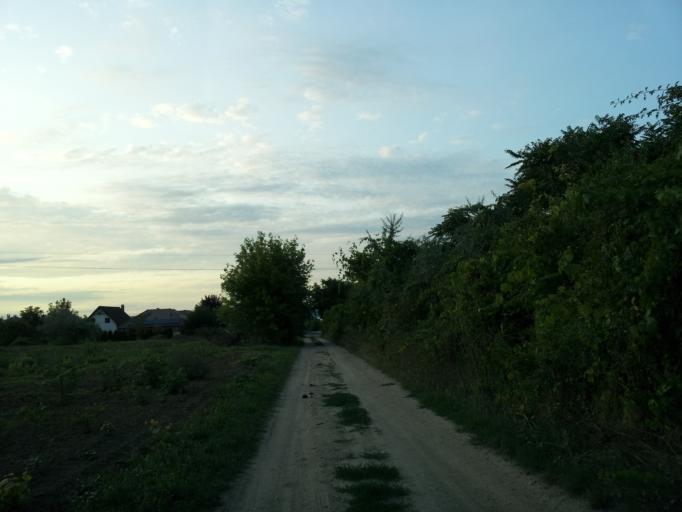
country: HU
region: Somogy
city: Zamardi
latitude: 46.8735
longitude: 17.9486
